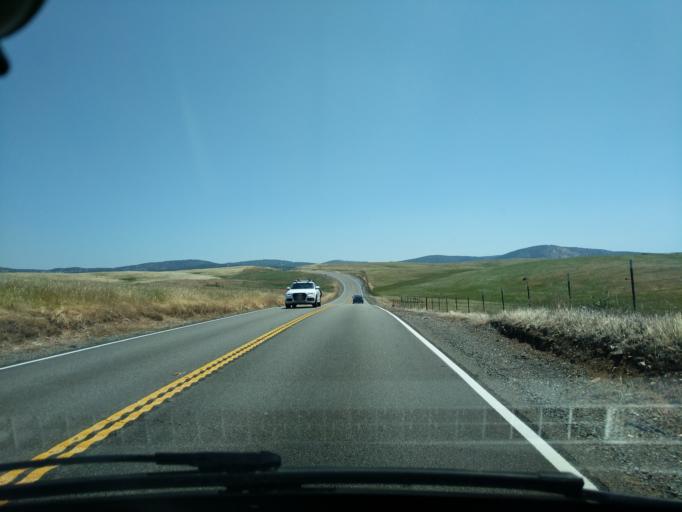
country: US
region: California
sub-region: Stanislaus County
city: East Oakdale
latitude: 37.9373
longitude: -120.7873
